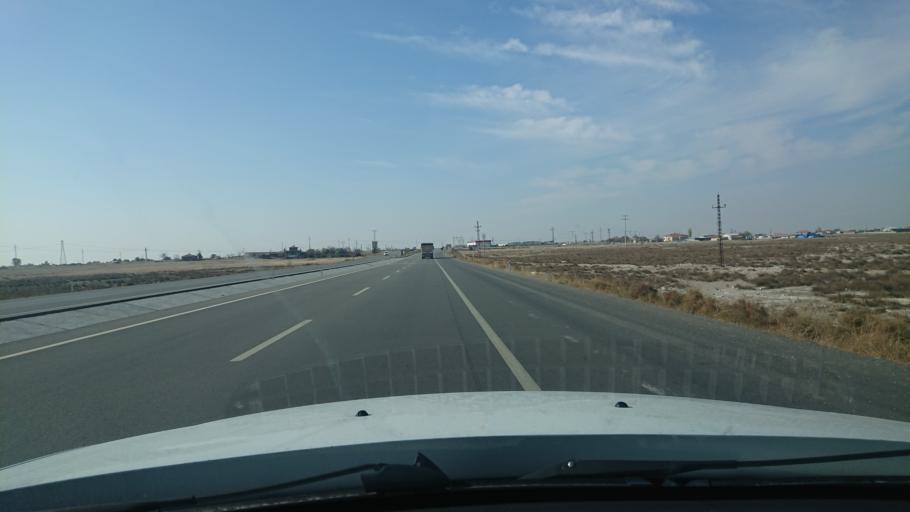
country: TR
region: Aksaray
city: Sultanhani
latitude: 38.2532
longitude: 33.4863
